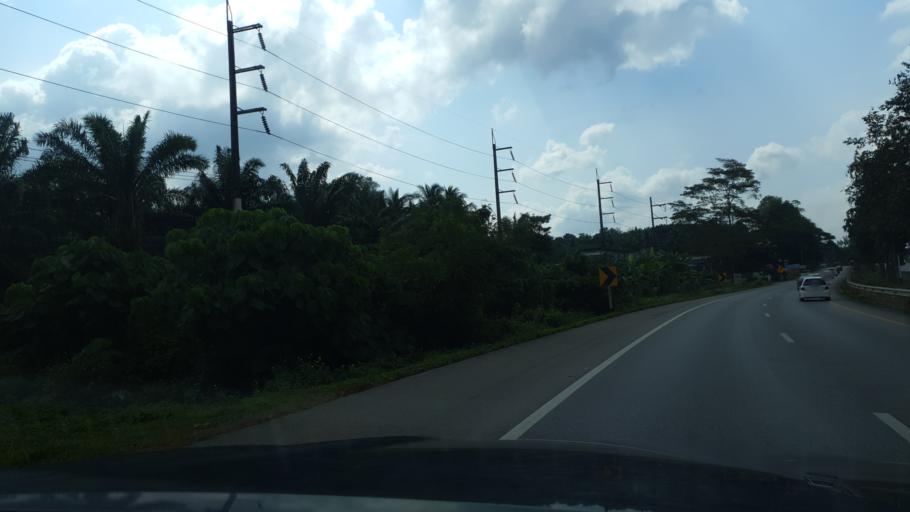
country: TH
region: Chumphon
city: Tha Sae
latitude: 10.6408
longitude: 99.1847
